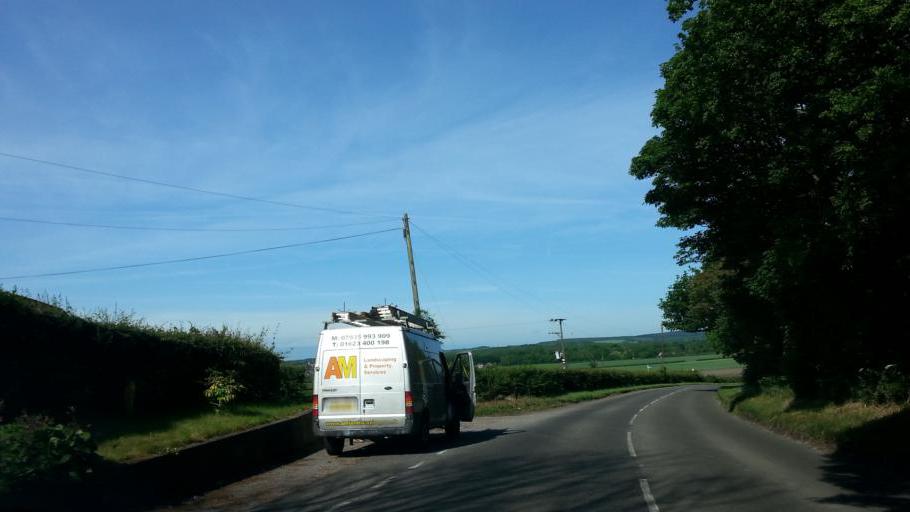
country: GB
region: England
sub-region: Nottinghamshire
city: Hucknall
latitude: 53.0522
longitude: -1.1632
